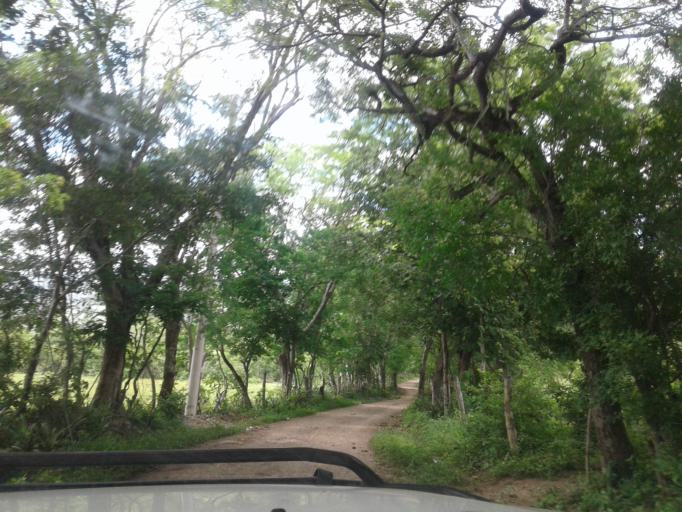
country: NI
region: Leon
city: Santa Rosa del Penon
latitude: 12.8662
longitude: -86.2392
